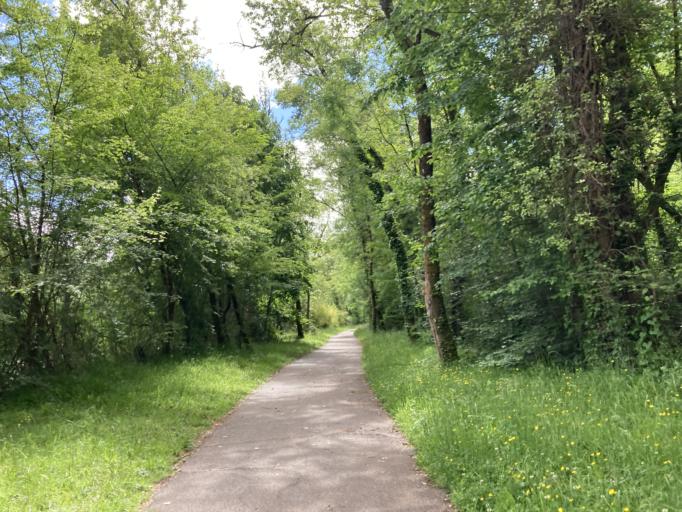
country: FR
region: Aquitaine
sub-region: Departement des Pyrenees-Atlantiques
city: Billere
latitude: 43.3013
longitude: -0.4266
